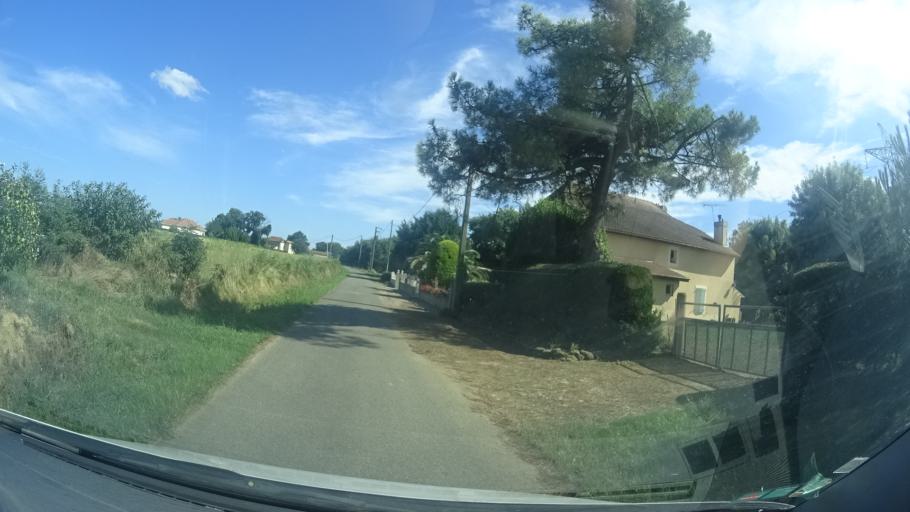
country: FR
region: Aquitaine
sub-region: Departement des Pyrenees-Atlantiques
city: Mont
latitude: 43.5029
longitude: -0.6781
